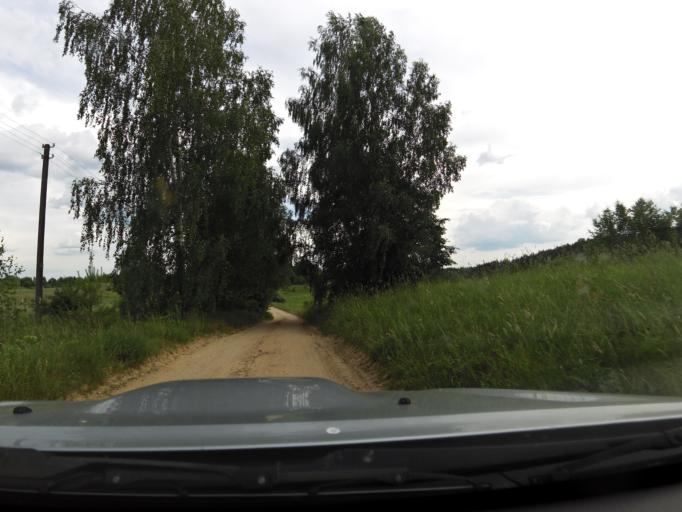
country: LT
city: Grigiskes
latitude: 54.7885
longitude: 25.0128
